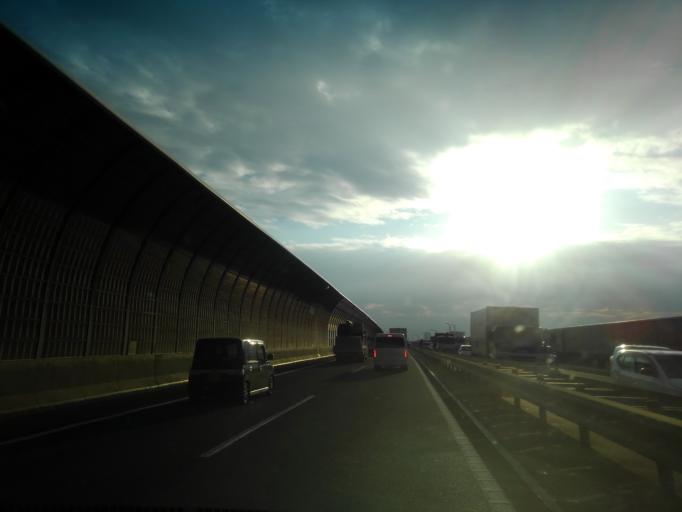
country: JP
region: Saitama
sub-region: Kawaguchi-shi
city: Hatogaya-honcho
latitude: 35.8497
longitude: 139.7626
